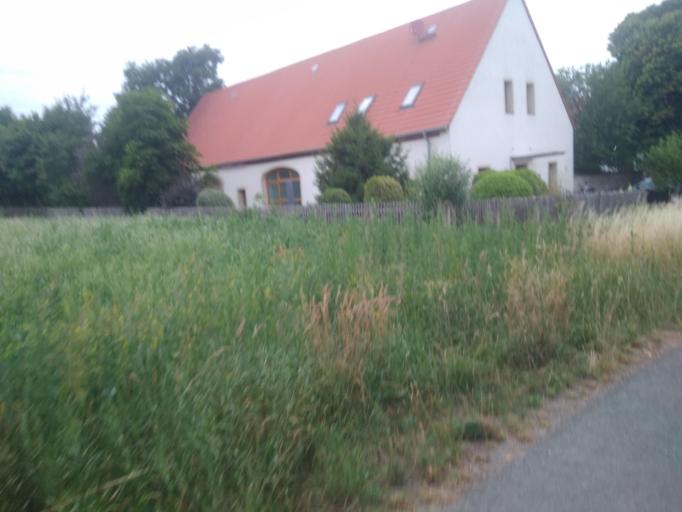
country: DE
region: Saxony
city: Freital
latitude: 51.0420
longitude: 13.6288
